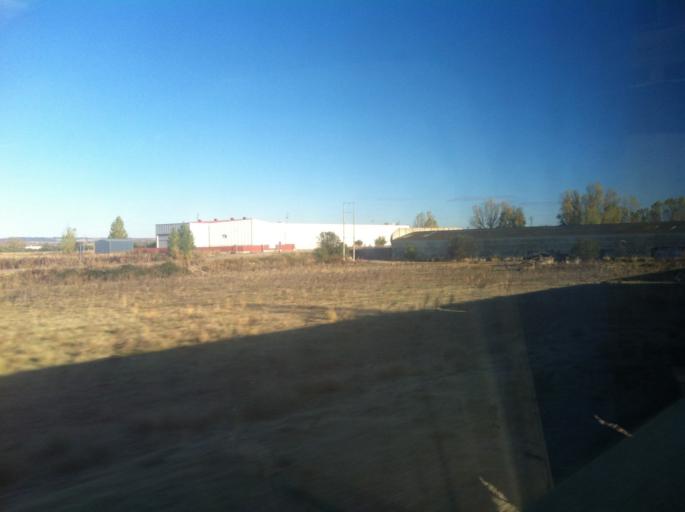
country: ES
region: Castille and Leon
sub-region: Provincia de Valladolid
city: Cabezon
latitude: 41.7514
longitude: -4.6376
